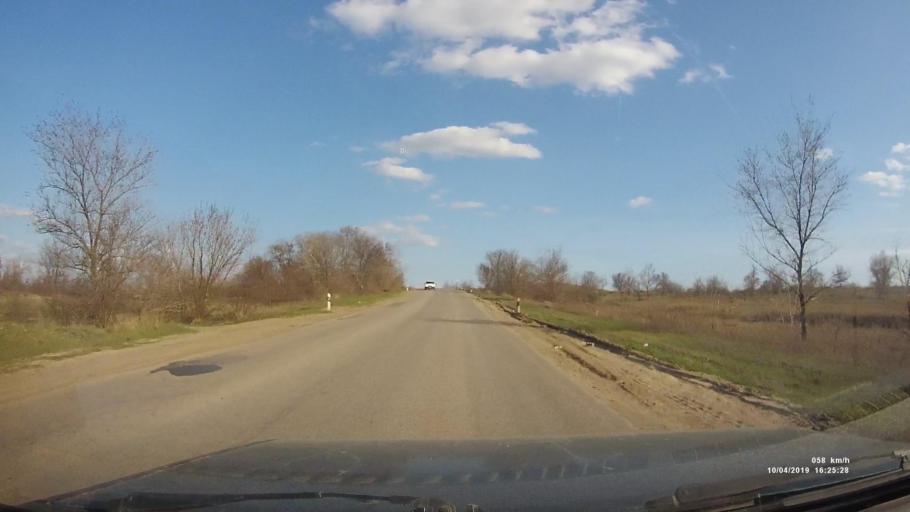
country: RU
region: Rostov
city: Staraya Stanitsa
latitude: 48.2926
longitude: 40.3239
